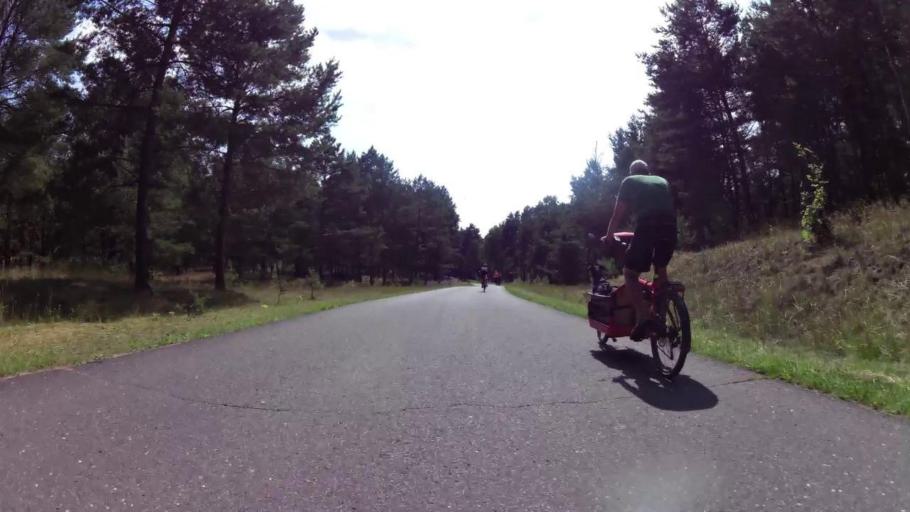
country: PL
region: West Pomeranian Voivodeship
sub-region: Powiat choszczenski
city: Drawno
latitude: 53.3557
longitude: 15.7036
